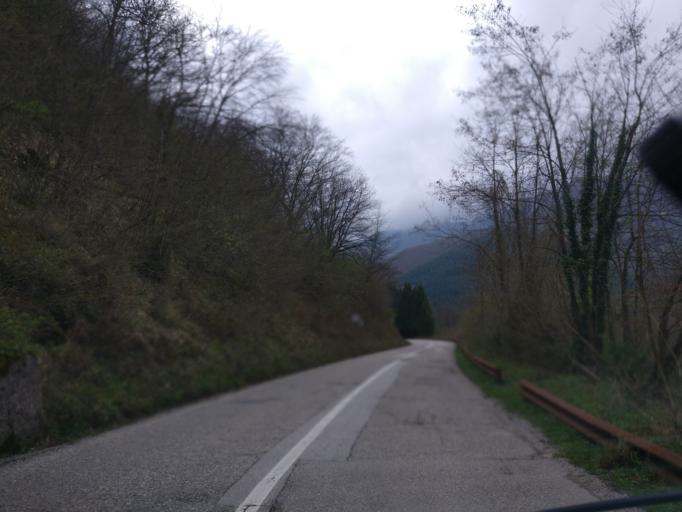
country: BA
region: Republika Srpska
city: Foca
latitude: 43.4639
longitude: 18.7477
